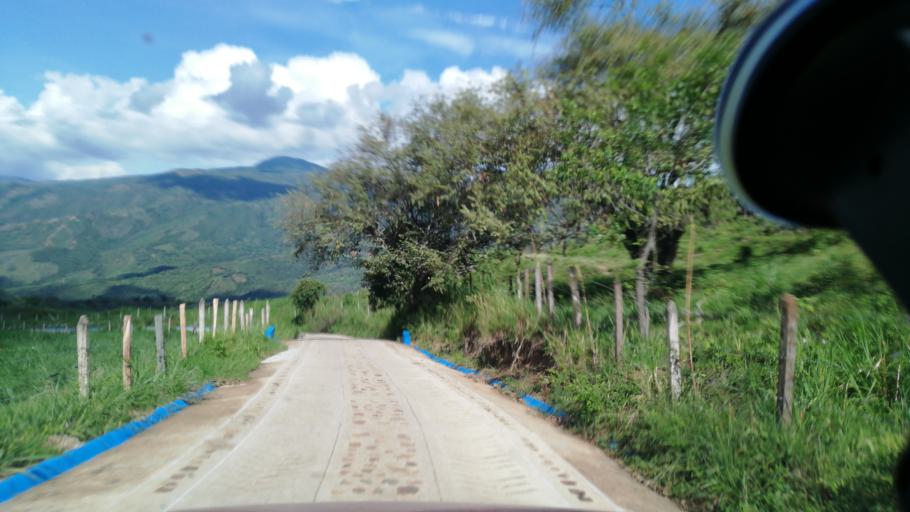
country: CO
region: Cundinamarca
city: Quipile
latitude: 4.7758
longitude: -74.6150
